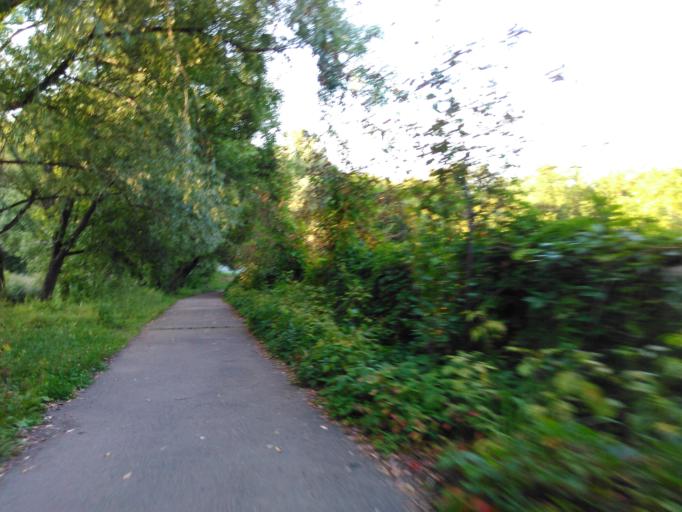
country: RU
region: Moscow
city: Vorob'yovo
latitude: 55.7272
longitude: 37.5190
